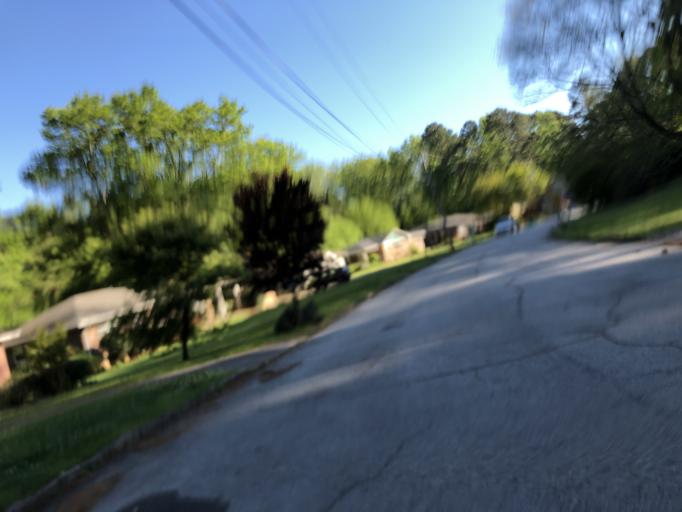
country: US
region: Georgia
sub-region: DeKalb County
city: North Decatur
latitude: 33.8081
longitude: -84.2881
